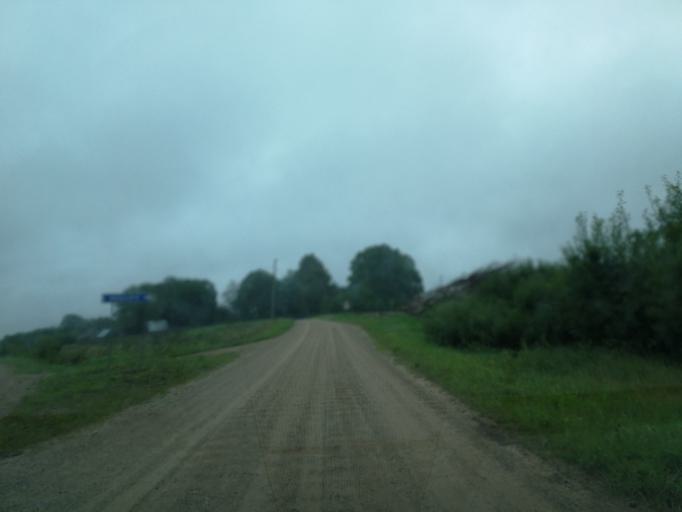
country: LV
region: Preilu Rajons
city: Jaunaglona
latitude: 56.3446
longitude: 27.0164
